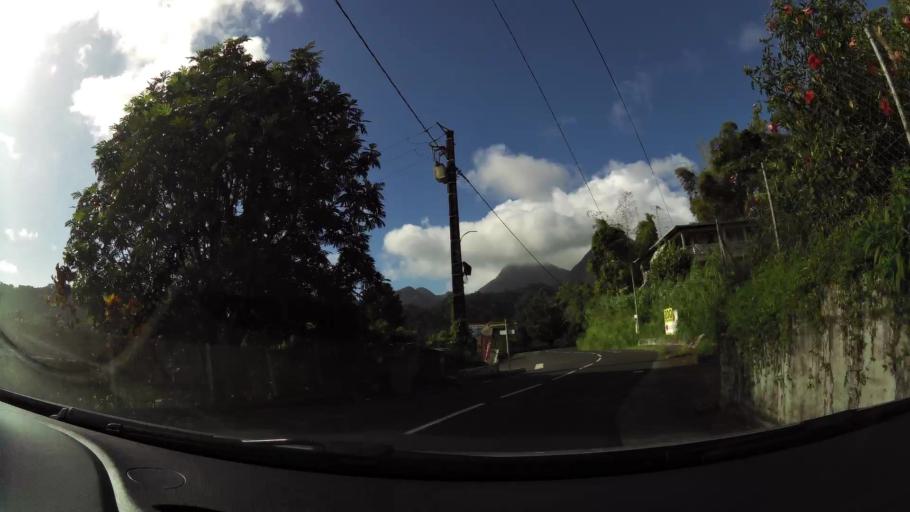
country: MQ
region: Martinique
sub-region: Martinique
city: Saint-Joseph
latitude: 14.6726
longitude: -61.0910
